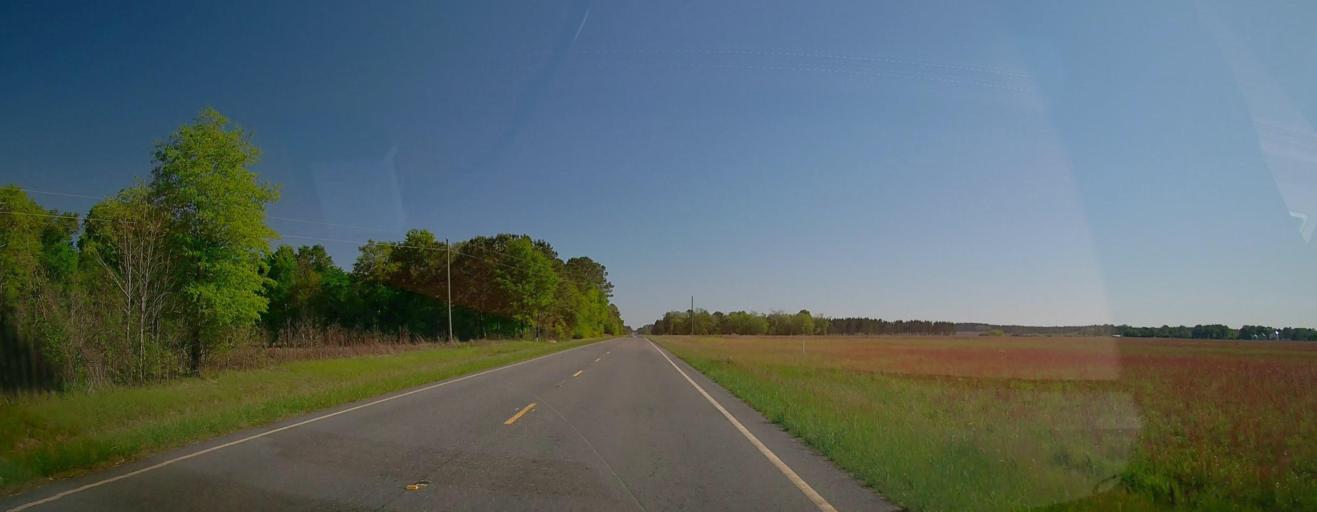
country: US
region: Georgia
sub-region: Wilcox County
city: Rochelle
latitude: 32.0835
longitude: -83.5034
